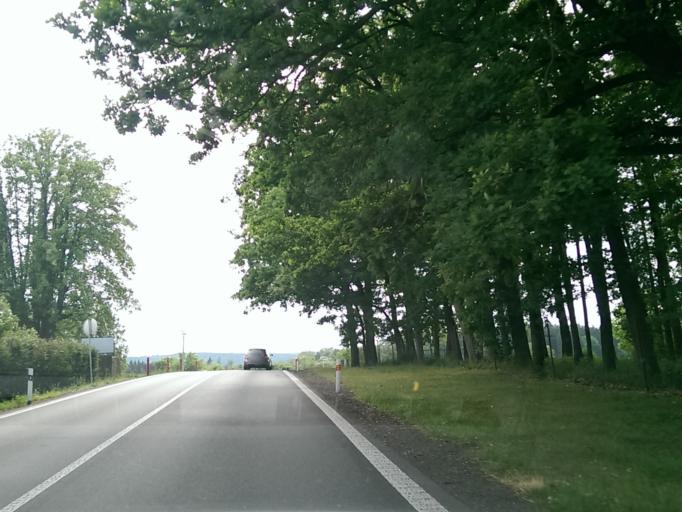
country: CZ
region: Kralovehradecky
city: Horice
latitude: 50.3992
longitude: 15.6776
